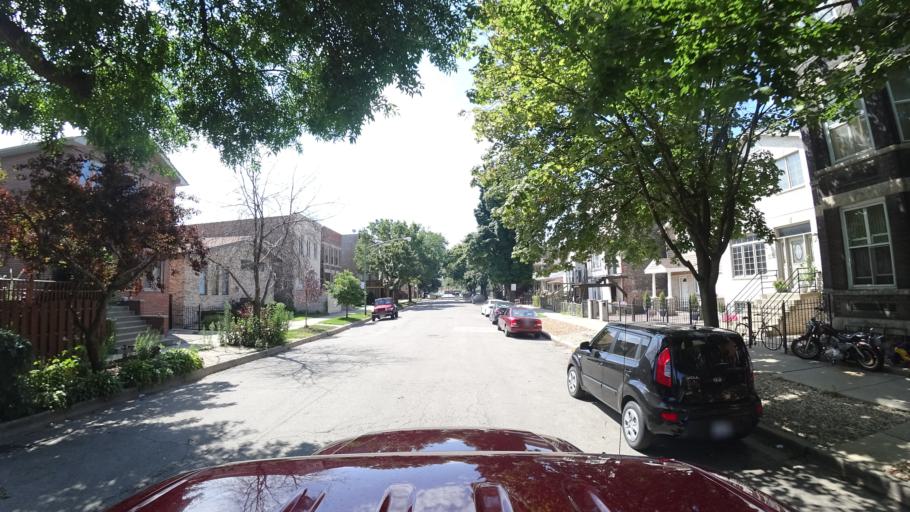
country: US
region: Illinois
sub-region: Cook County
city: Chicago
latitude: 41.8252
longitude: -87.6399
